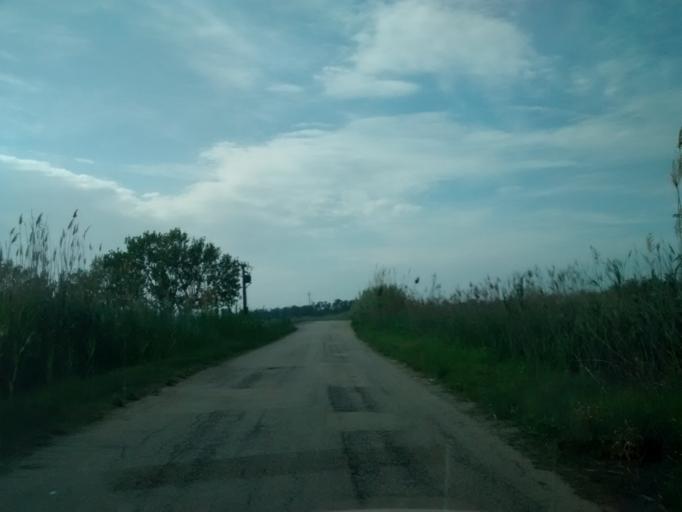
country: ES
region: Catalonia
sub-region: Provincia de Tarragona
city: Deltebre
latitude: 40.6943
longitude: 0.8390
